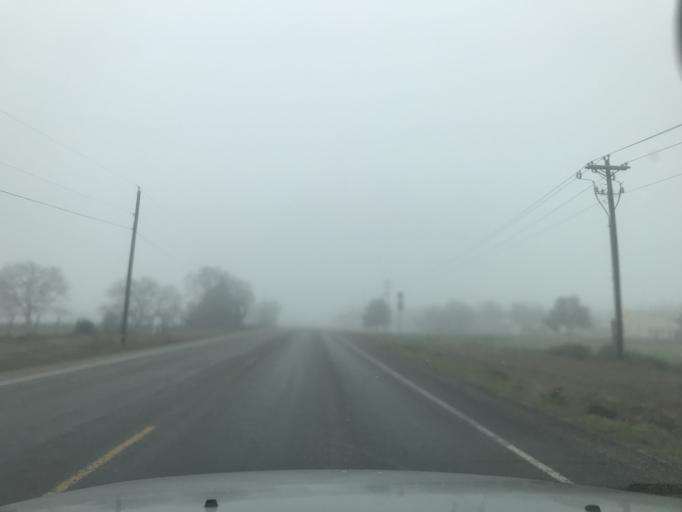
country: US
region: Texas
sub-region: Rockwall County
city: Royse City
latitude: 33.0069
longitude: -96.2943
